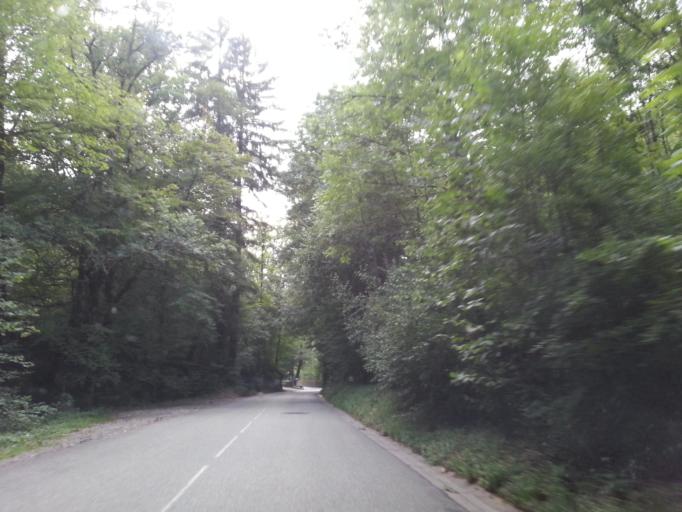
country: FR
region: Rhone-Alpes
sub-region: Departement de la Haute-Savoie
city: Menthon-Saint-Bernard
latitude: 45.8670
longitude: 6.2085
